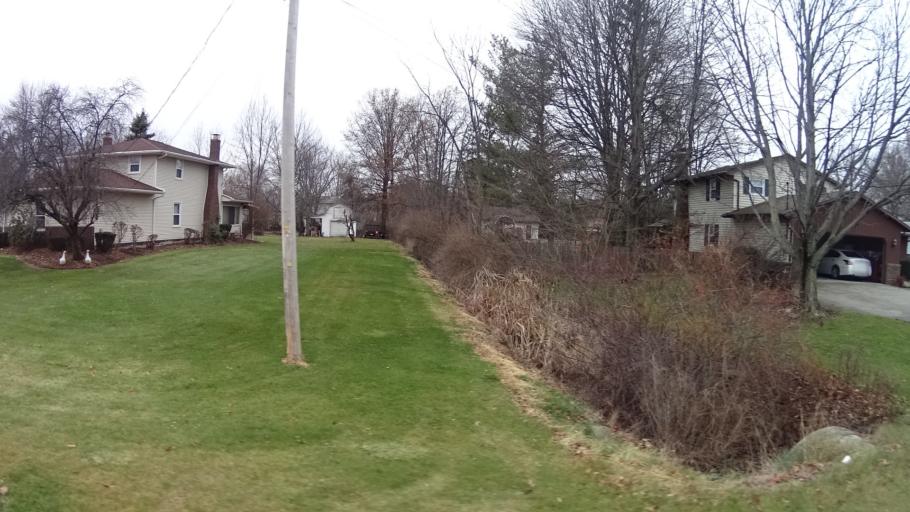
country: US
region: Ohio
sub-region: Lorain County
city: North Ridgeville
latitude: 41.3663
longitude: -81.9957
